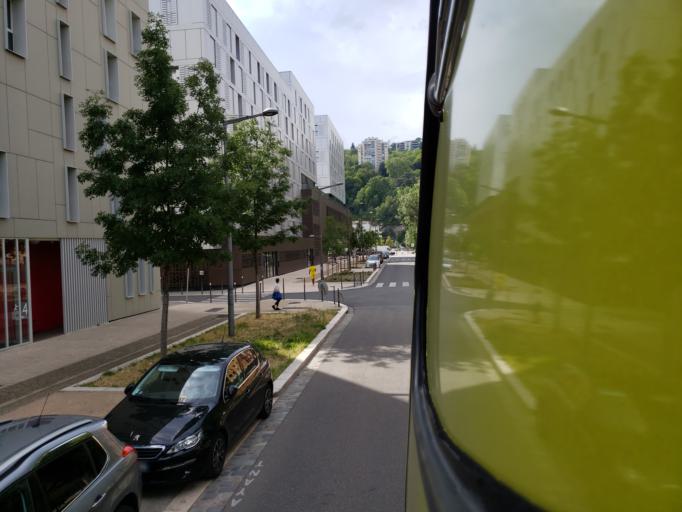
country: FR
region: Rhone-Alpes
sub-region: Departement du Rhone
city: La Mulatiere
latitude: 45.7450
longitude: 4.8185
